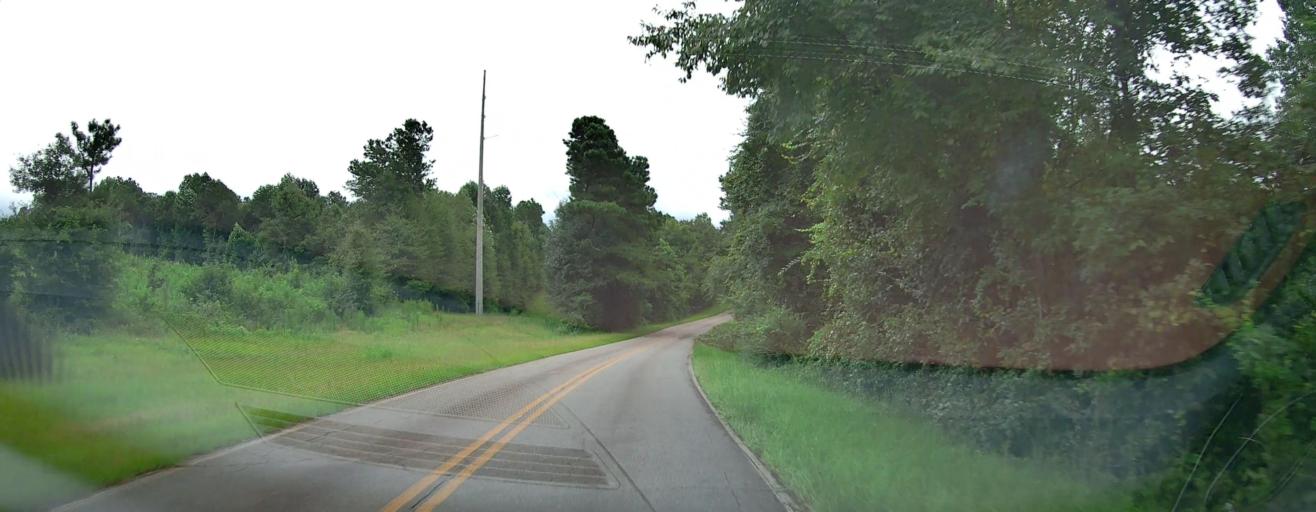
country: US
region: Georgia
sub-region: Bibb County
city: Macon
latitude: 32.7895
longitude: -83.5156
